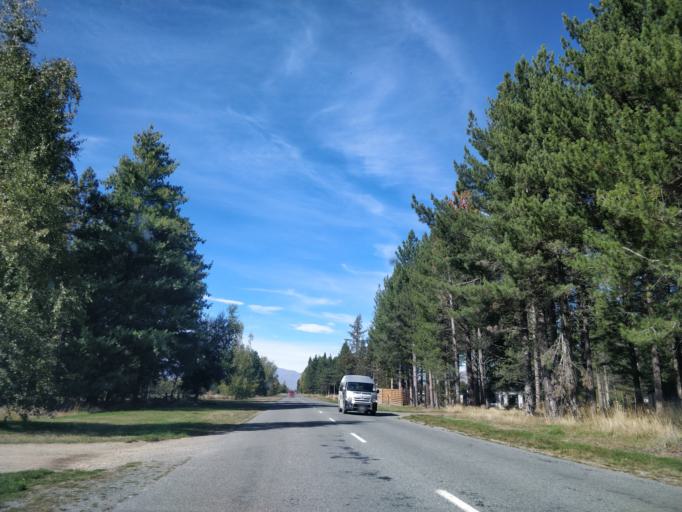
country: NZ
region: Canterbury
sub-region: Timaru District
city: Pleasant Point
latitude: -44.2482
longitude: 170.0966
